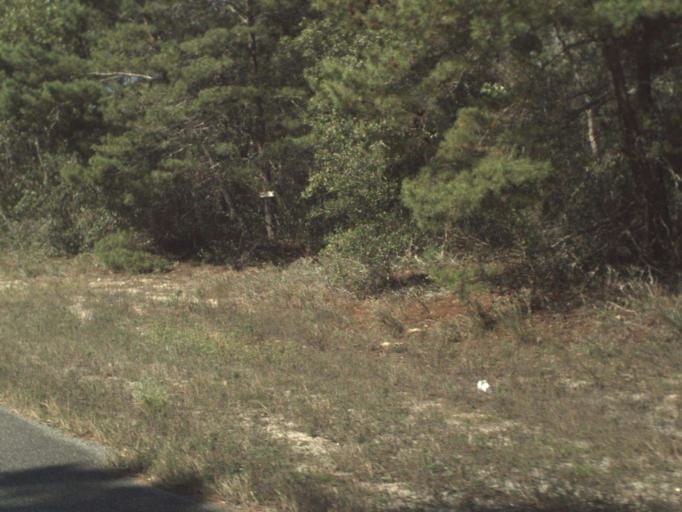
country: US
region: Florida
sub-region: Franklin County
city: Carrabelle
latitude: 29.9331
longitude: -84.4479
